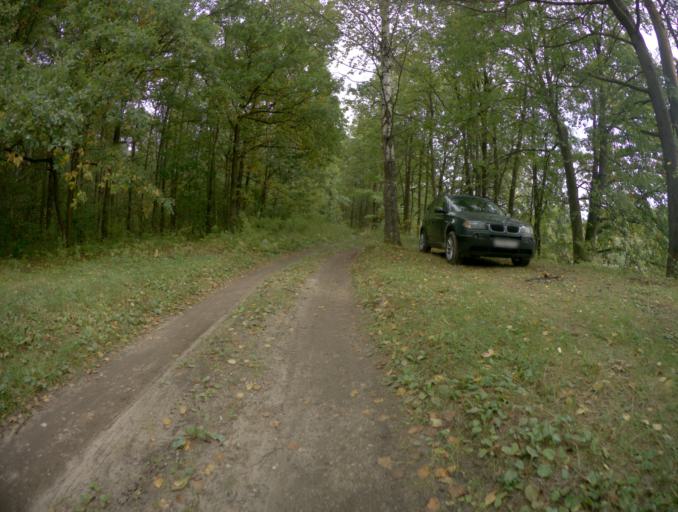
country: RU
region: Vladimir
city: Raduzhnyy
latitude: 56.0521
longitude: 40.3019
